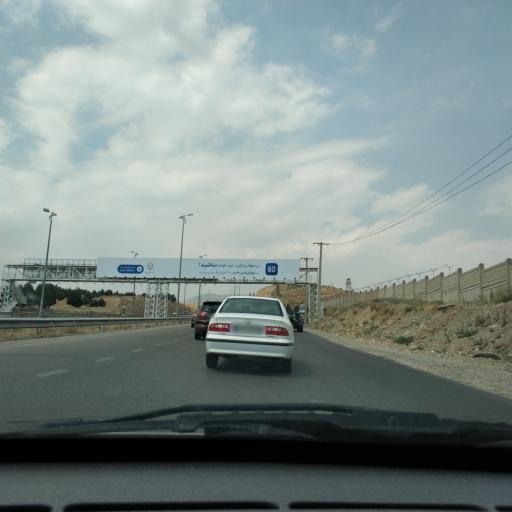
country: IR
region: Tehran
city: Tajrish
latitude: 35.7842
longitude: 51.5653
